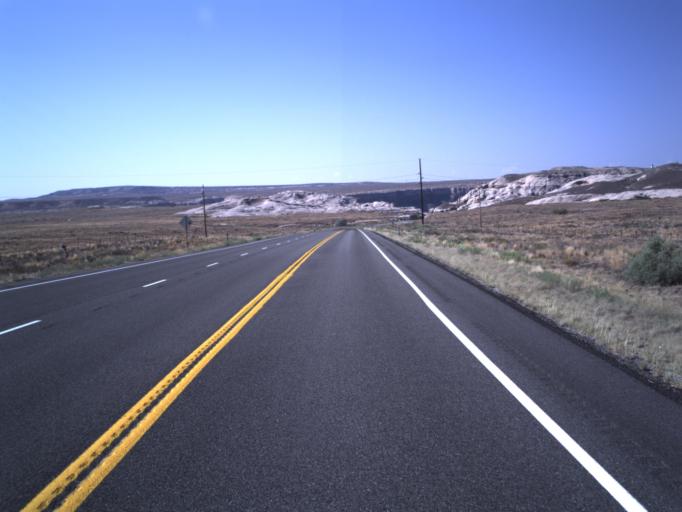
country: US
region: Utah
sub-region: San Juan County
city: Blanding
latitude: 37.3058
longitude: -109.5290
